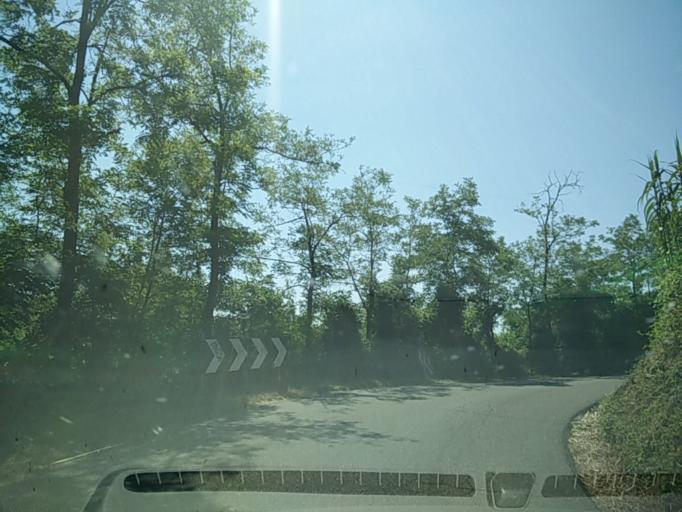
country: IT
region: Lombardy
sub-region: Provincia di Pavia
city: Godiasco
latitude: 44.9009
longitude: 9.0459
